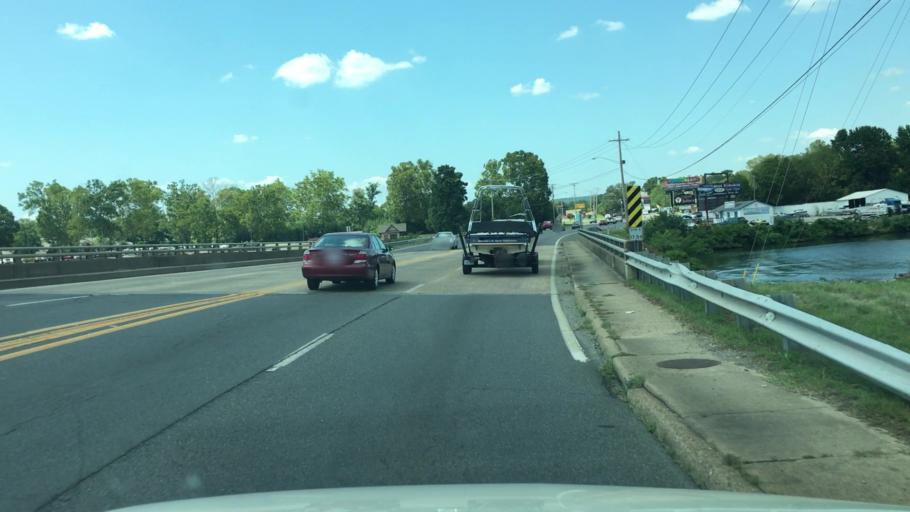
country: US
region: Arkansas
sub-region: Garland County
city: Piney
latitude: 34.4959
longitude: -93.1214
